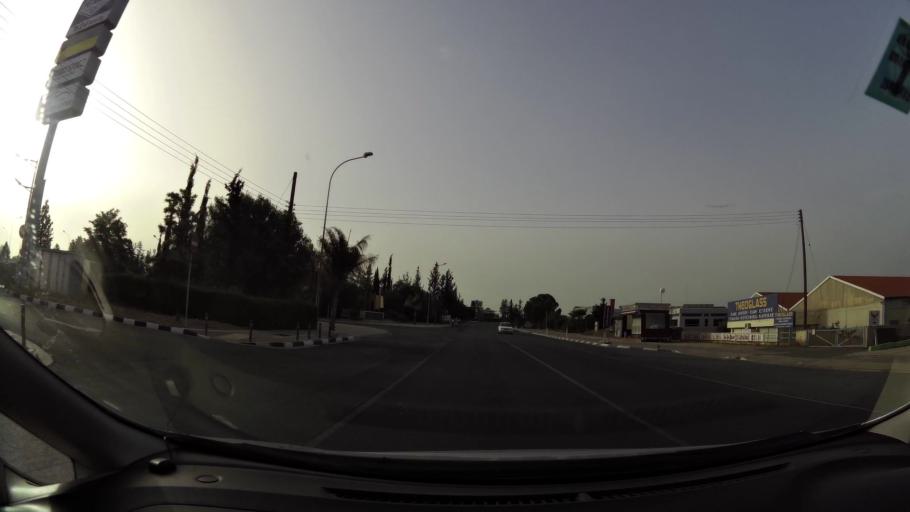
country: CY
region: Lefkosia
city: Geri
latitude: 35.0783
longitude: 33.3813
